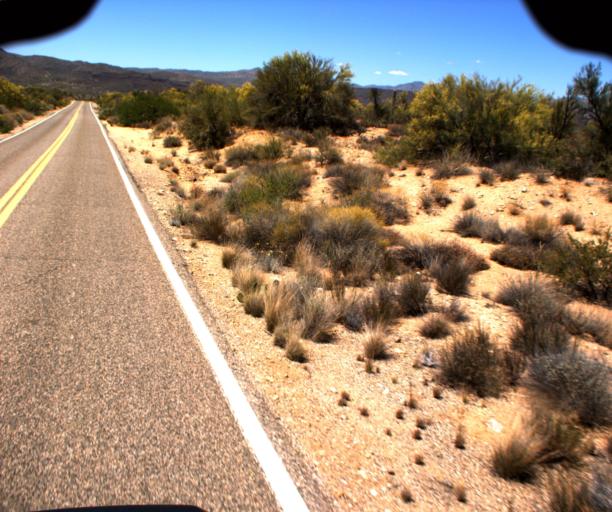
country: US
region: Arizona
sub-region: Yavapai County
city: Bagdad
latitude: 34.4668
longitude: -113.0470
